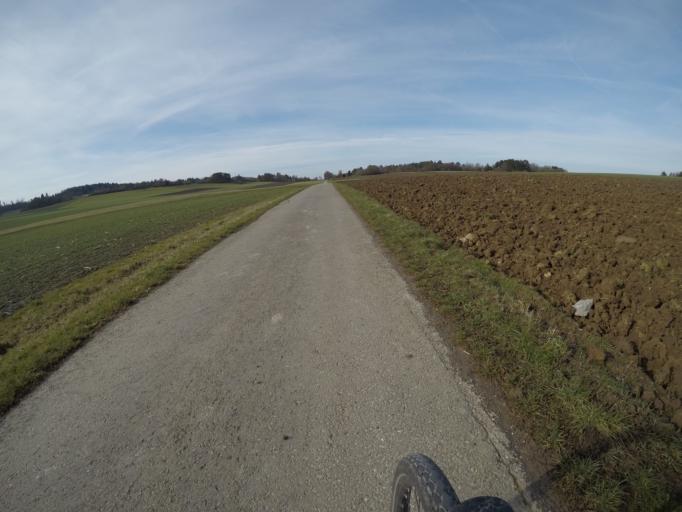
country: DE
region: Baden-Wuerttemberg
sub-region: Karlsruhe Region
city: Althengstett
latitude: 48.6938
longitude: 8.7921
